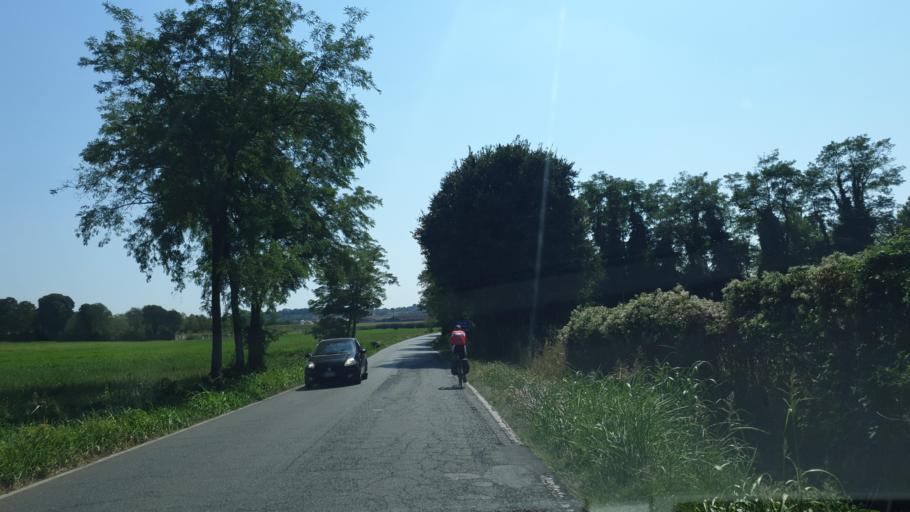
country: IT
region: Lombardy
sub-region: Provincia di Brescia
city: Carzago Riviera
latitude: 45.4929
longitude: 10.4667
